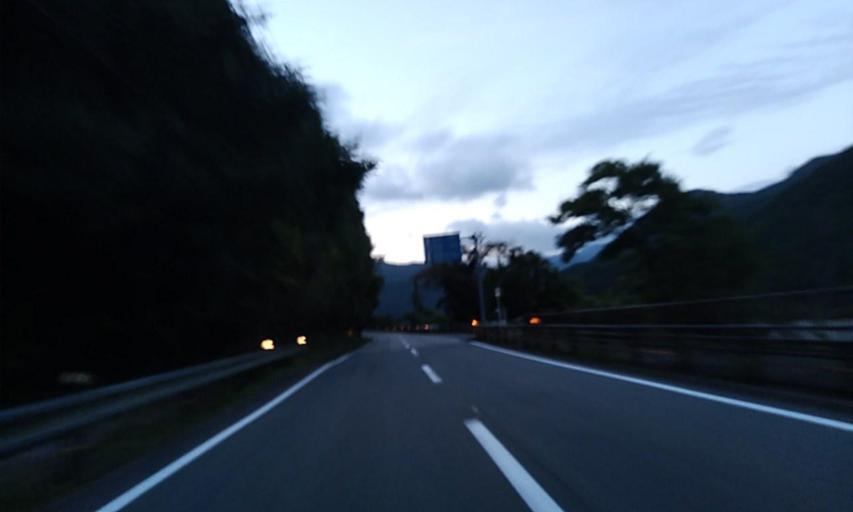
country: JP
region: Wakayama
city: Shingu
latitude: 33.7292
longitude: 135.9490
